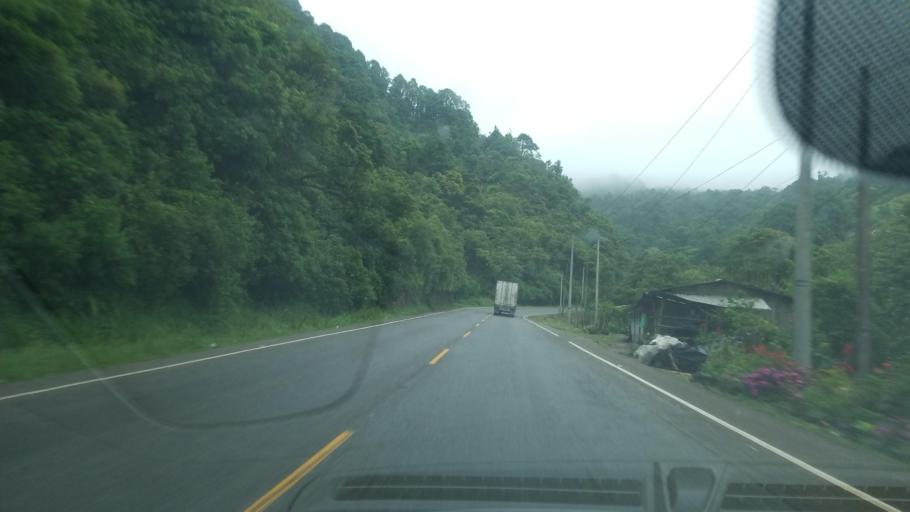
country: HN
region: Ocotepeque
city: La Labor
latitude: 14.4692
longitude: -89.0667
